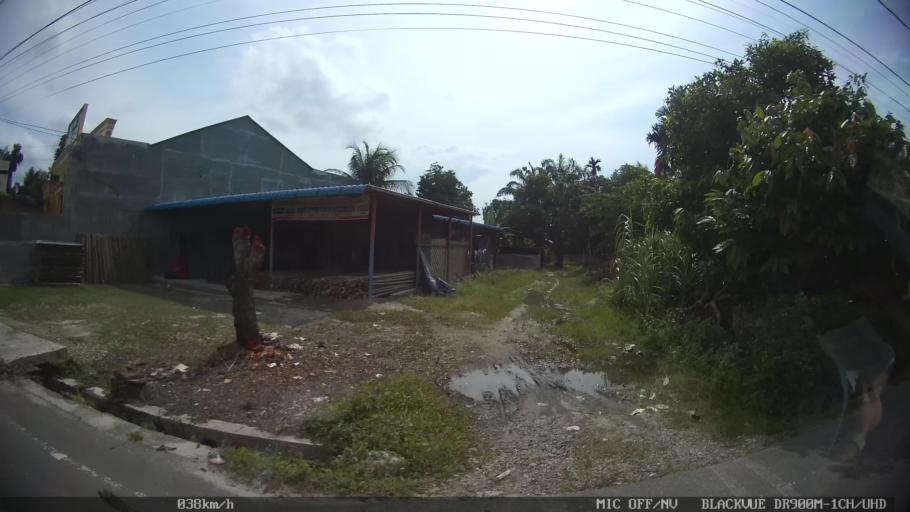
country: ID
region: North Sumatra
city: Percut
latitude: 3.6034
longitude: 98.8571
